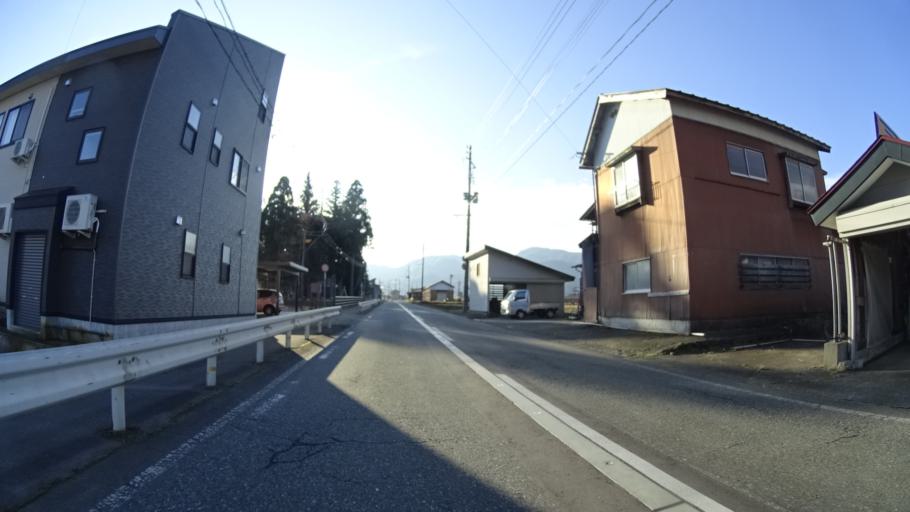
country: JP
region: Niigata
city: Shiozawa
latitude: 37.0081
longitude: 138.8453
